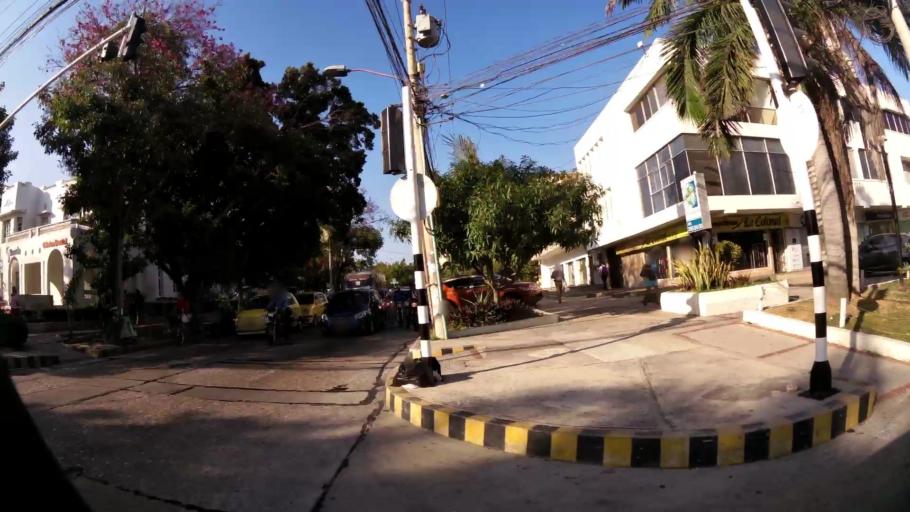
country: CO
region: Atlantico
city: Barranquilla
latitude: 10.9993
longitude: -74.8044
